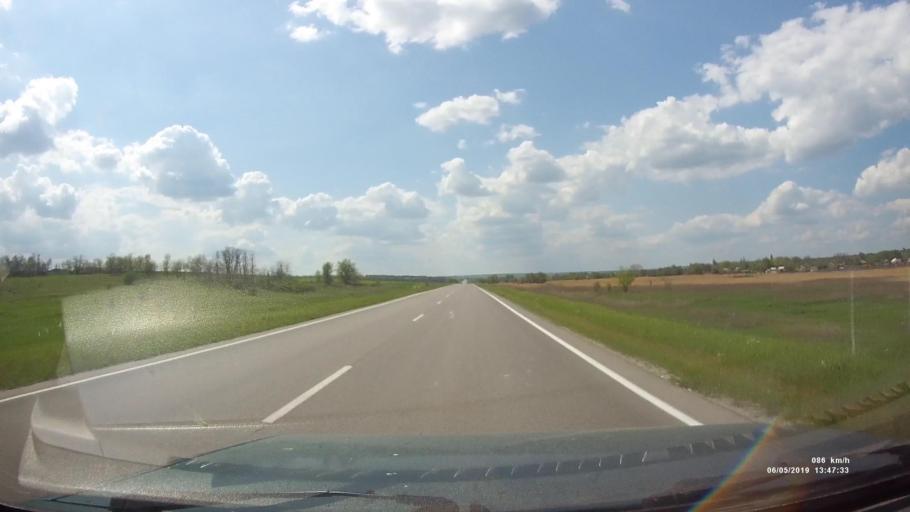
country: RU
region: Rostov
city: Melikhovskaya
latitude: 47.6572
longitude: 40.5609
